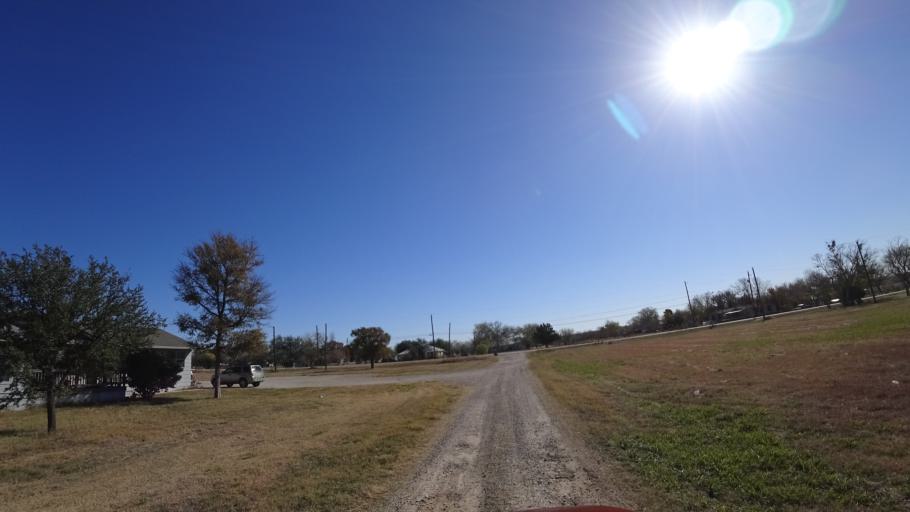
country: US
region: Texas
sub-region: Travis County
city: Garfield
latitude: 30.1180
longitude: -97.6476
